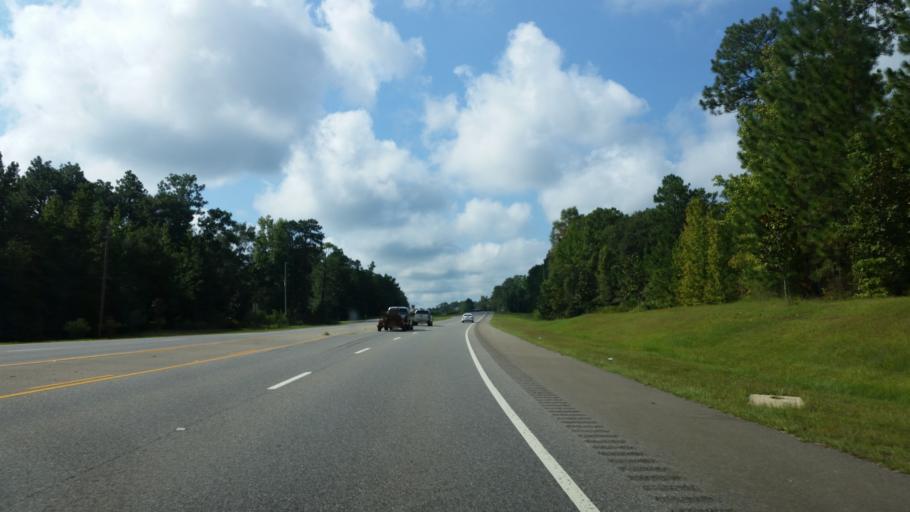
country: US
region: Alabama
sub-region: Baldwin County
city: Bay Minette
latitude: 30.9505
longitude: -87.7619
